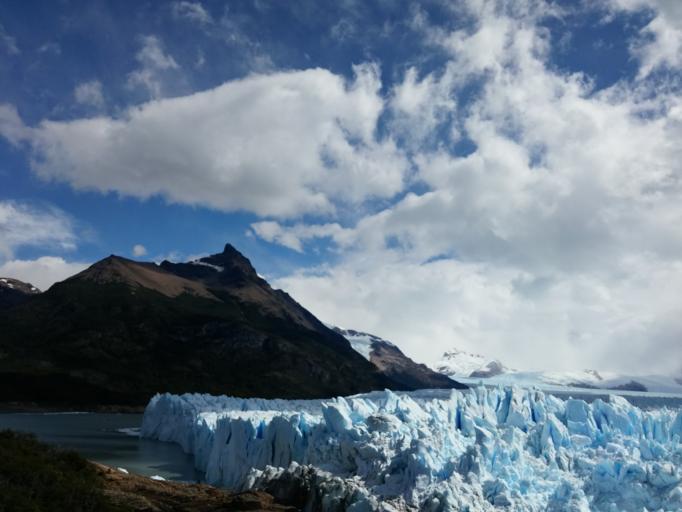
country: AR
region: Santa Cruz
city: El Calafate
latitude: -50.4716
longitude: -73.0332
